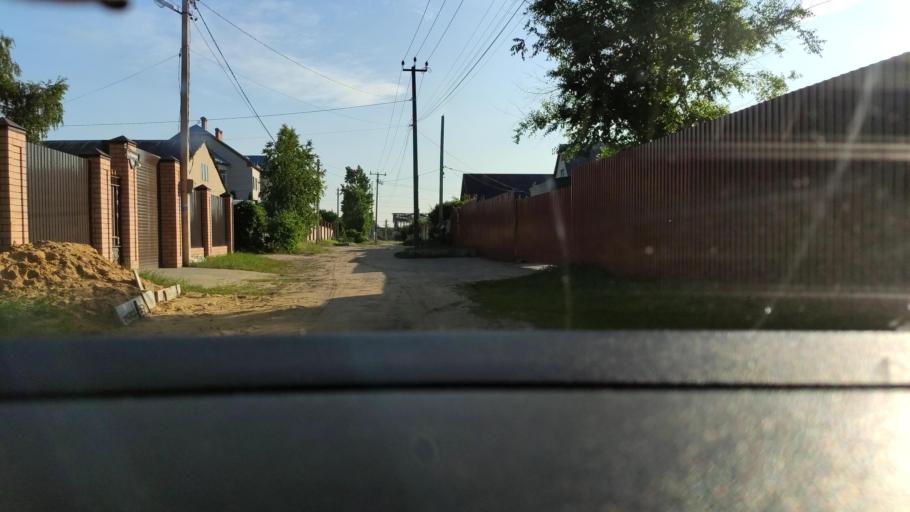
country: RU
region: Voronezj
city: Podgornoye
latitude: 51.7457
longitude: 39.1633
